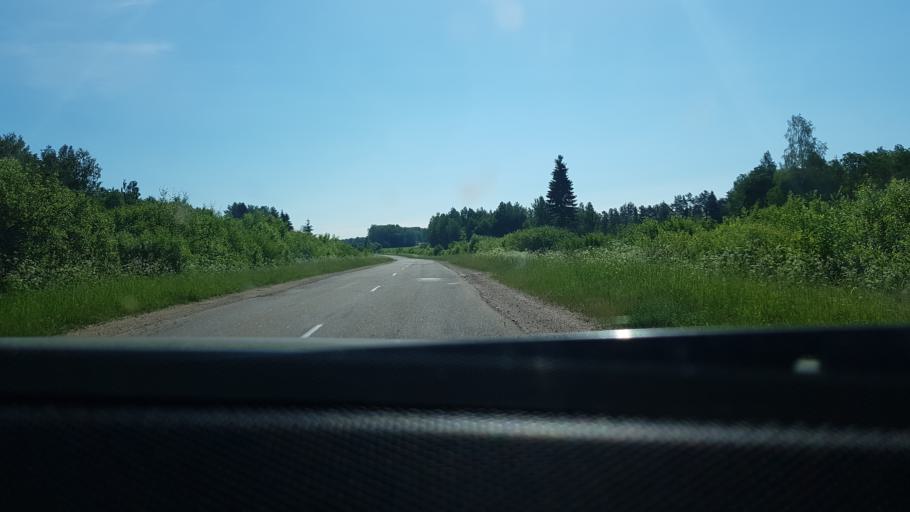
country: LV
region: Daugavpils
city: Daugavpils
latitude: 55.8166
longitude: 26.8133
